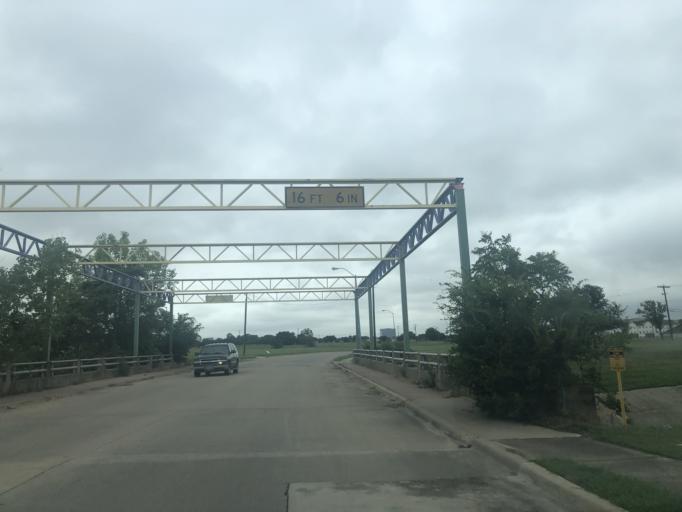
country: US
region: Texas
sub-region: Dallas County
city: Cockrell Hill
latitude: 32.7817
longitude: -96.8657
